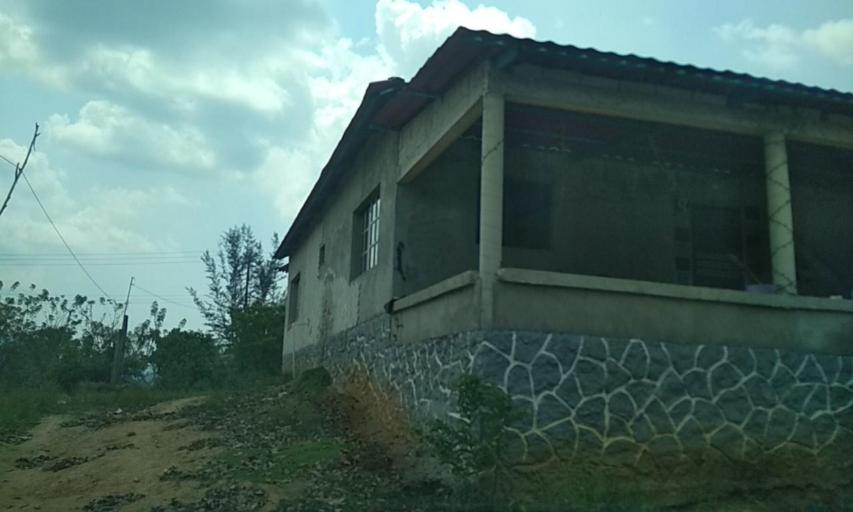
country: MX
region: Chiapas
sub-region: Tecpatan
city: Raudales Malpaso
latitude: 17.3488
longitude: -93.9639
